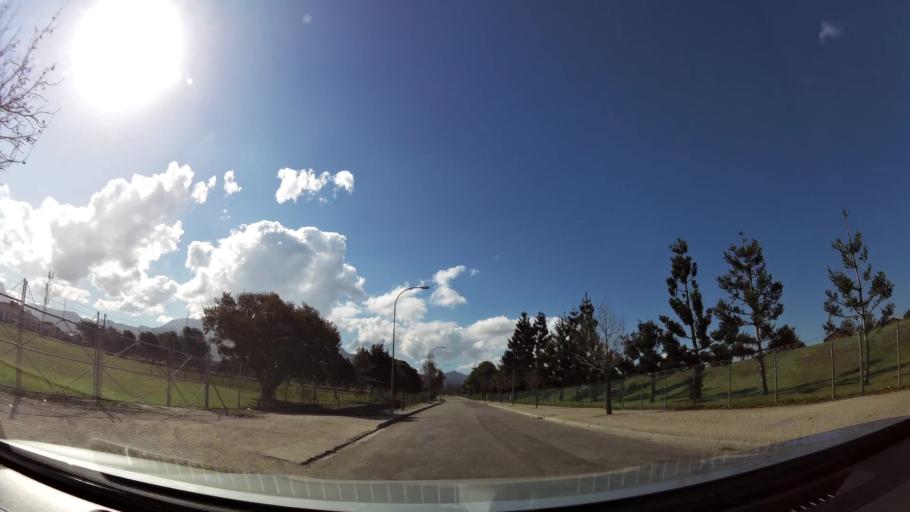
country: ZA
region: Western Cape
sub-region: Eden District Municipality
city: George
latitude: -33.9773
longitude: 22.4466
